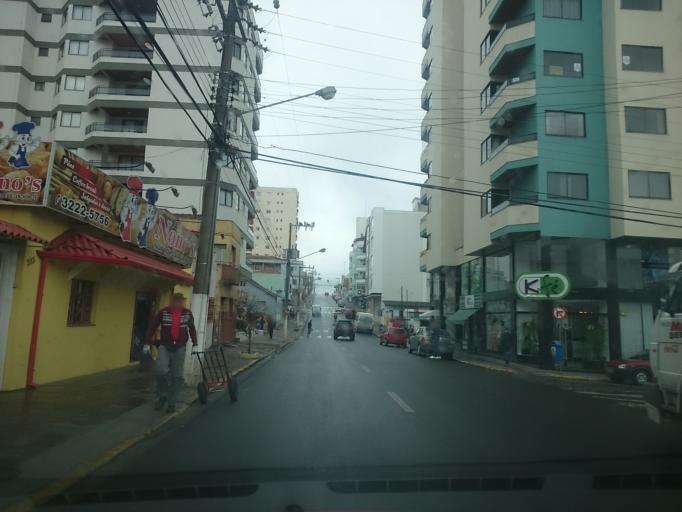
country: BR
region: Santa Catarina
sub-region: Lages
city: Lages
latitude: -27.8179
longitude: -50.3298
